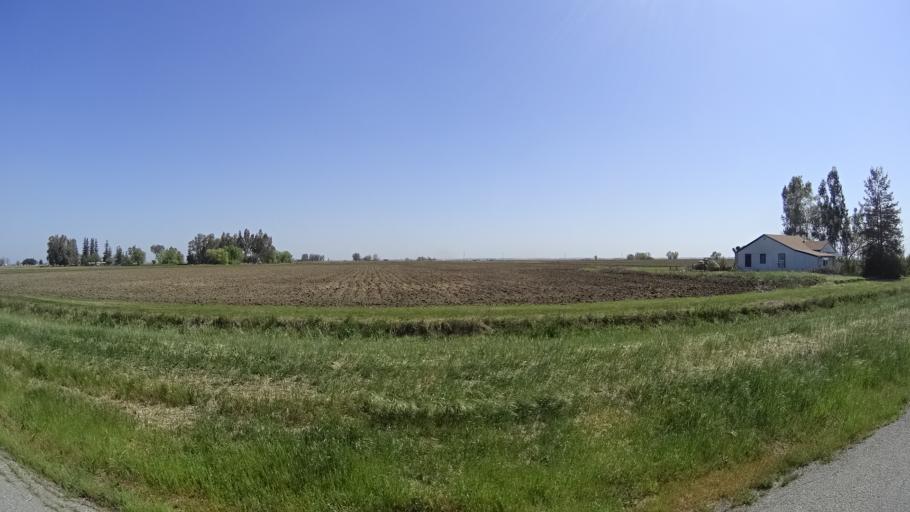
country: US
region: California
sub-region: Glenn County
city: Willows
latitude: 39.5406
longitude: -122.1035
